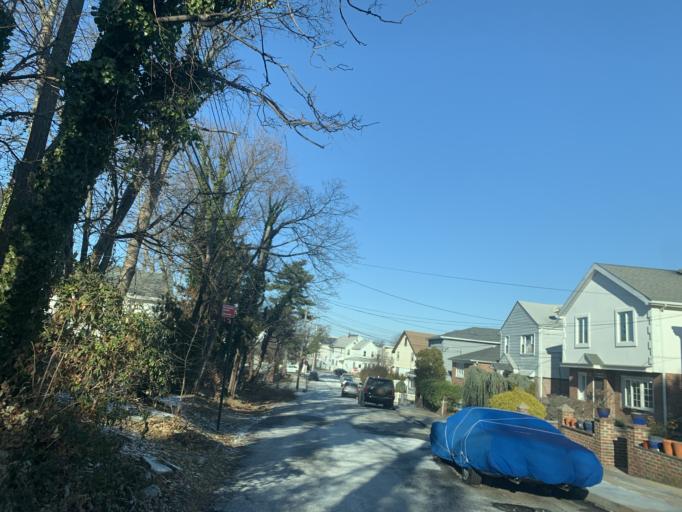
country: US
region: New York
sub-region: Nassau County
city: East Atlantic Beach
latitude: 40.7855
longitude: -73.8194
